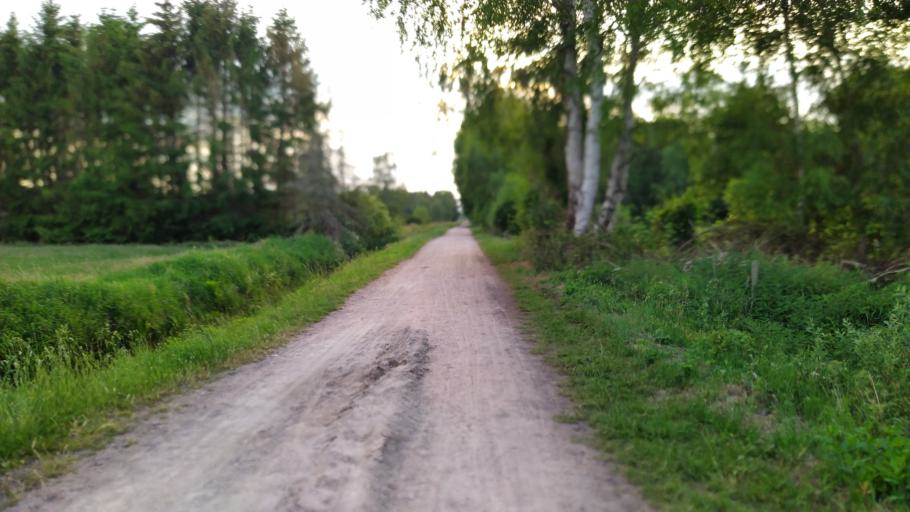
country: DE
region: Lower Saxony
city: Buxtehude
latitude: 53.4807
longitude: 9.6618
